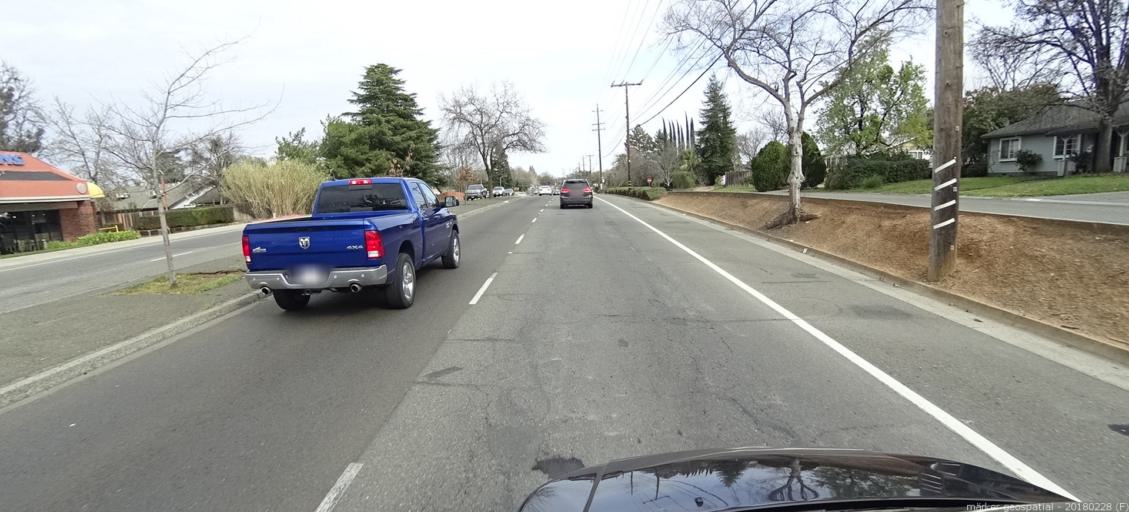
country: US
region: California
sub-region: Sacramento County
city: Fair Oaks
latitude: 38.6640
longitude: -121.2600
